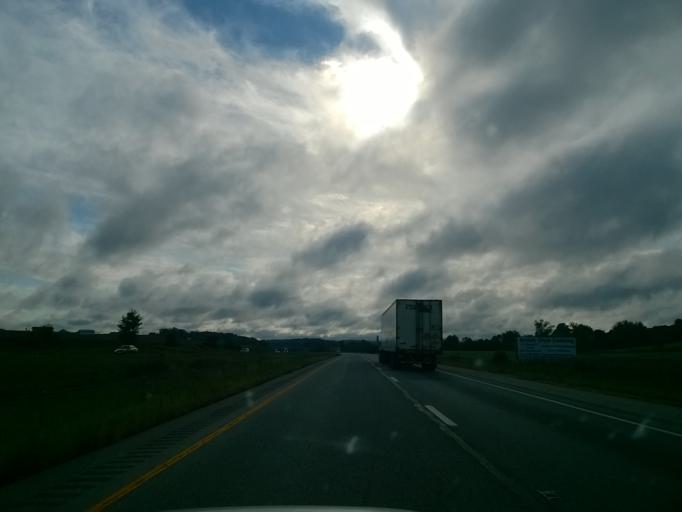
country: US
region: Indiana
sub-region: Dubois County
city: Ferdinand
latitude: 38.2314
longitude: -86.6601
